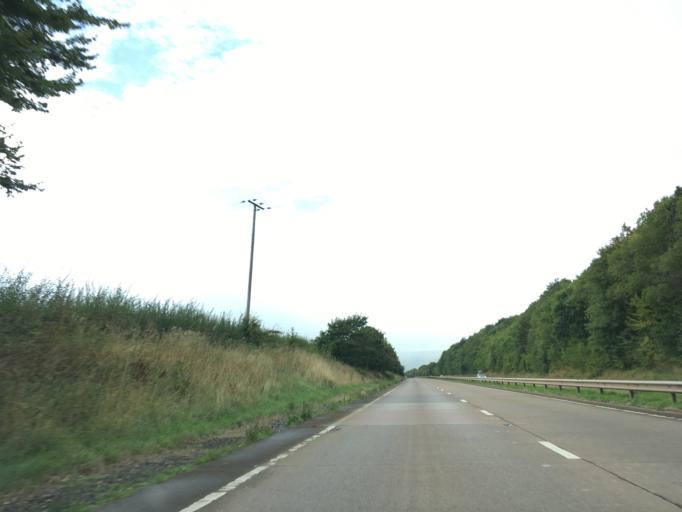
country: GB
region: Wales
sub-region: Monmouthshire
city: Llanarth
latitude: 51.7826
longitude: -2.9270
